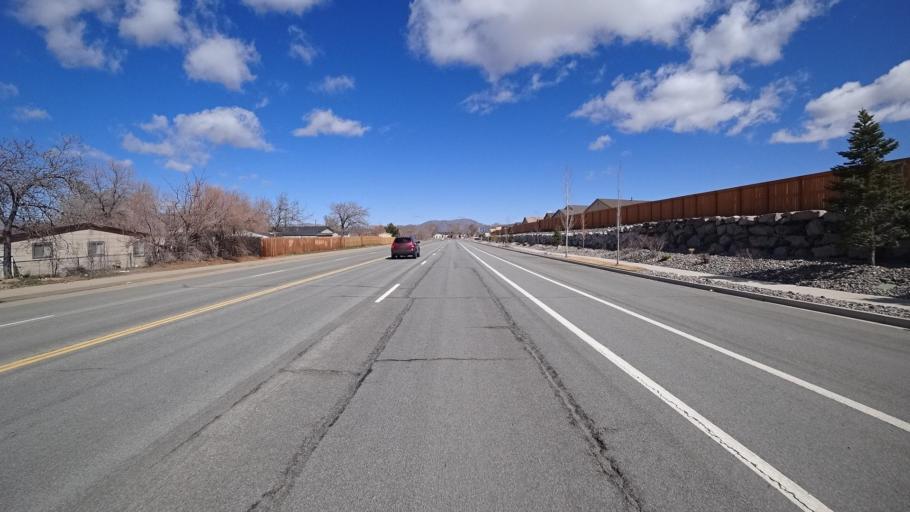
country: US
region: Nevada
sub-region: Washoe County
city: Lemmon Valley
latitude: 39.6501
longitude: -119.8759
